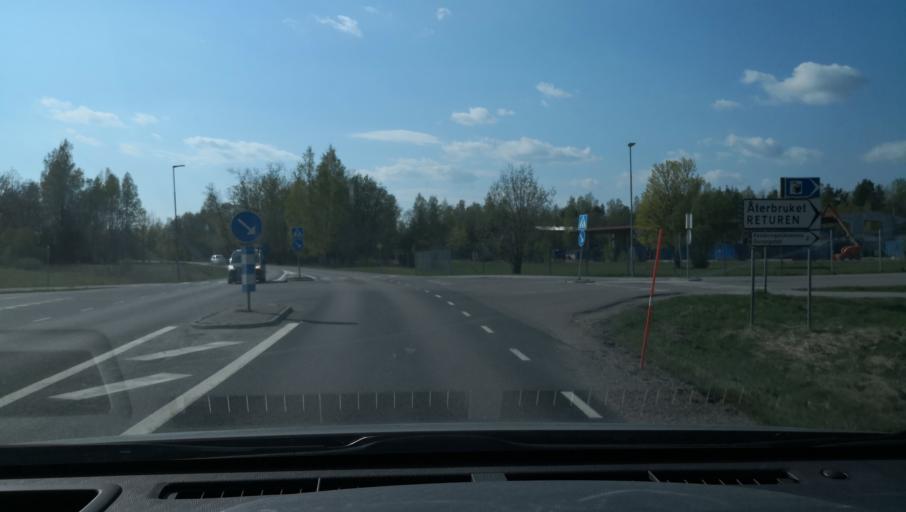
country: SE
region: Vaestmanland
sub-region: Sala Kommun
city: Sala
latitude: 59.9296
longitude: 16.5989
